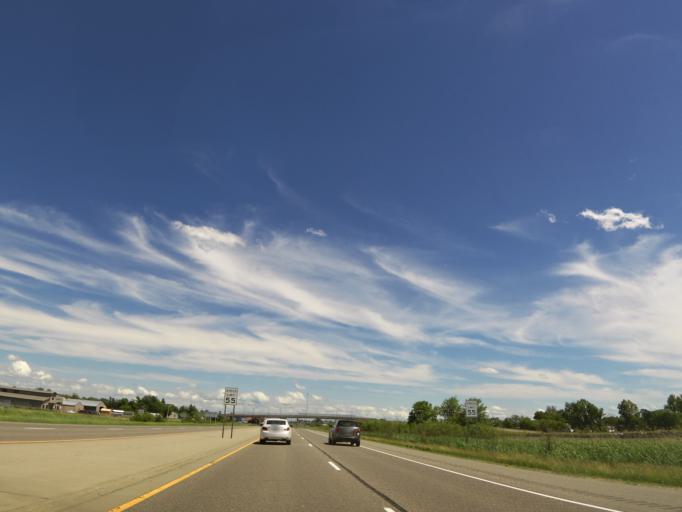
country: US
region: Minnesota
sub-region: Todd County
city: Staples
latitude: 46.3565
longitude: -94.8087
